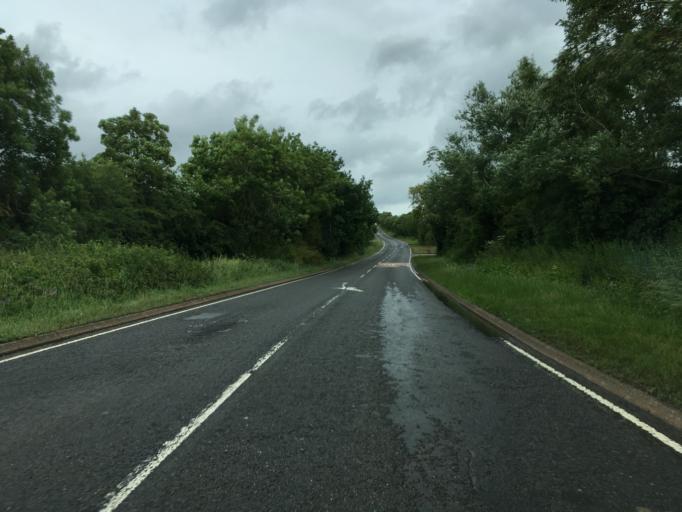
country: GB
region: England
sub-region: Warwickshire
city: Wellesbourne Mountford
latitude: 52.1272
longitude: -1.6021
